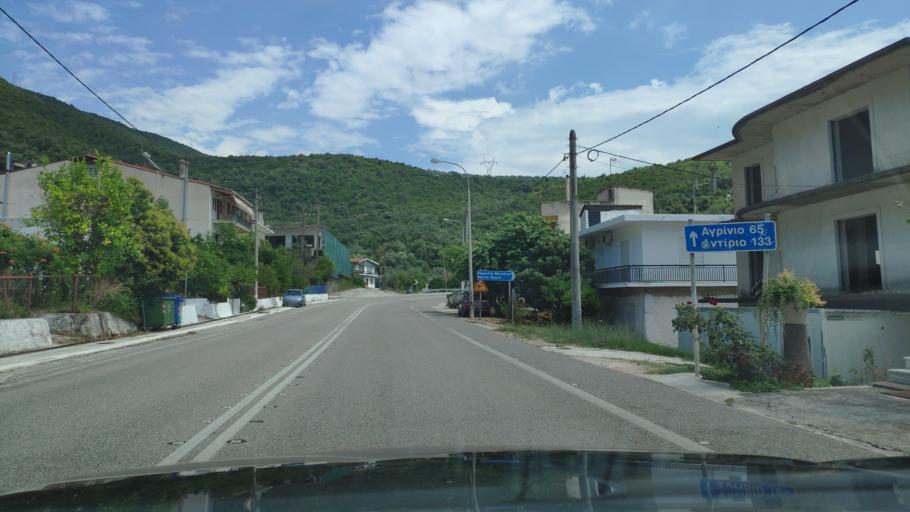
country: GR
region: West Greece
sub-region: Nomos Aitolias kai Akarnanias
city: Menidi
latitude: 39.0412
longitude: 21.1204
